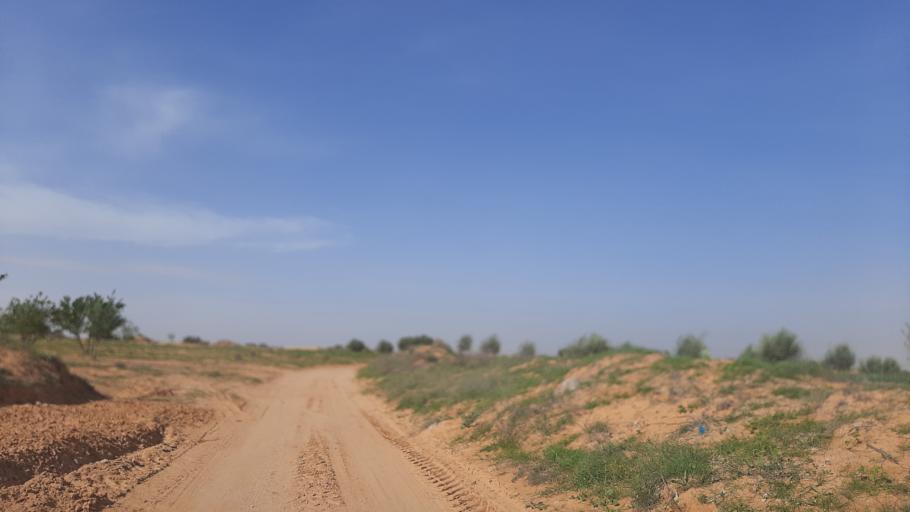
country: TN
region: Madanin
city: Zarzis
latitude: 33.4352
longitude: 10.8086
